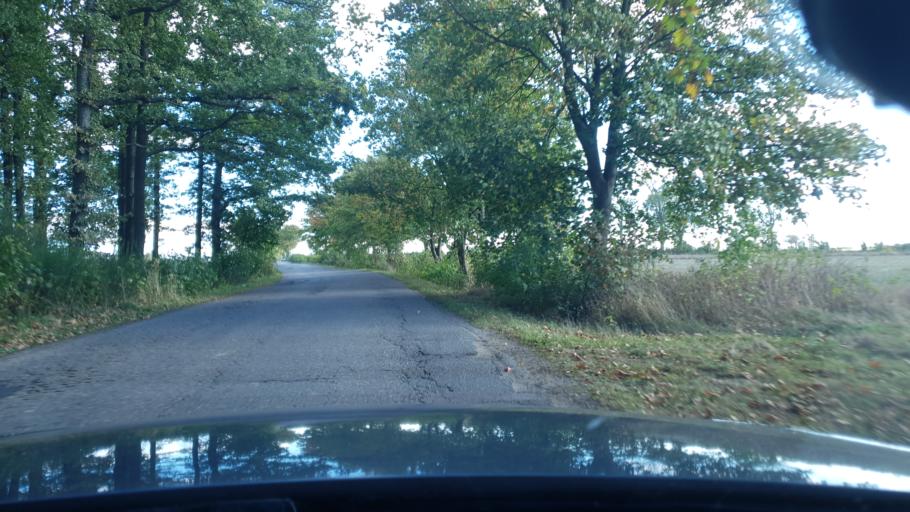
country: PL
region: Pomeranian Voivodeship
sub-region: Powiat pucki
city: Zelistrzewo
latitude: 54.6883
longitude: 18.4291
